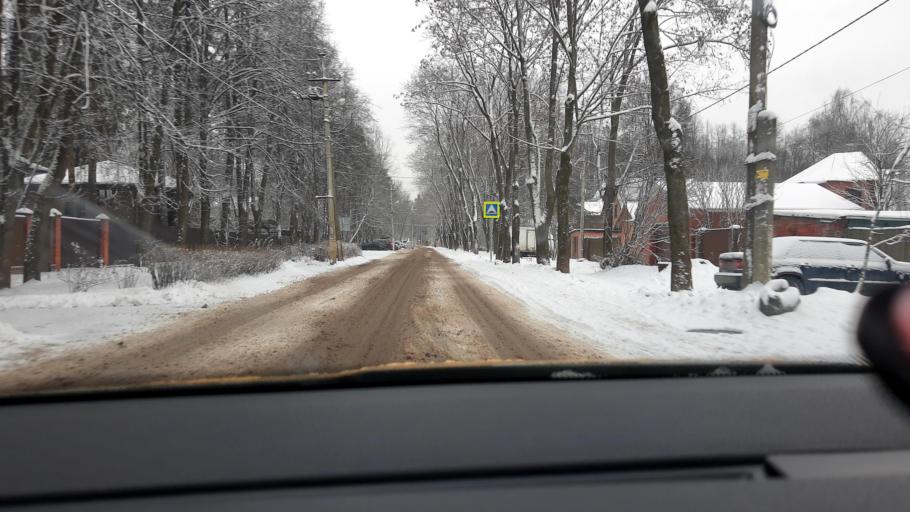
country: RU
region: Moskovskaya
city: Mamontovka
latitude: 55.9819
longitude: 37.8366
